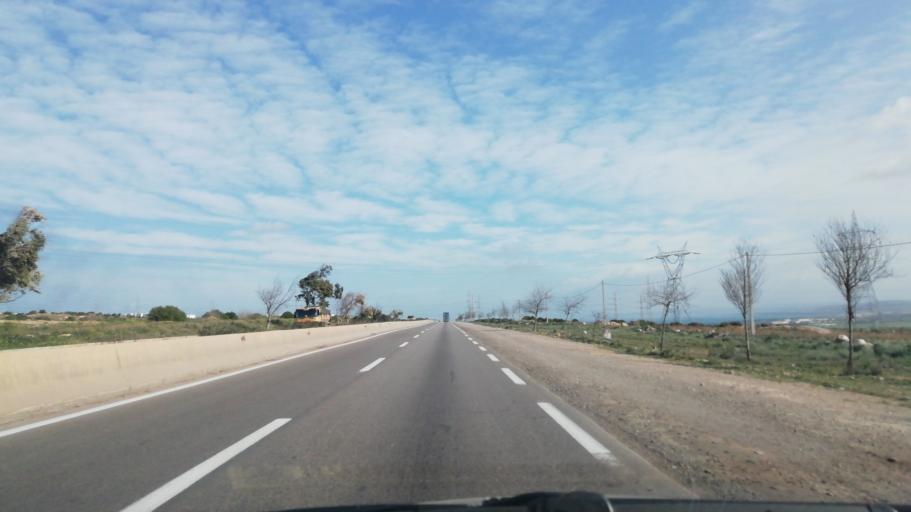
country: DZ
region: Oran
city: Ain el Bya
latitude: 35.7773
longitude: -0.1910
